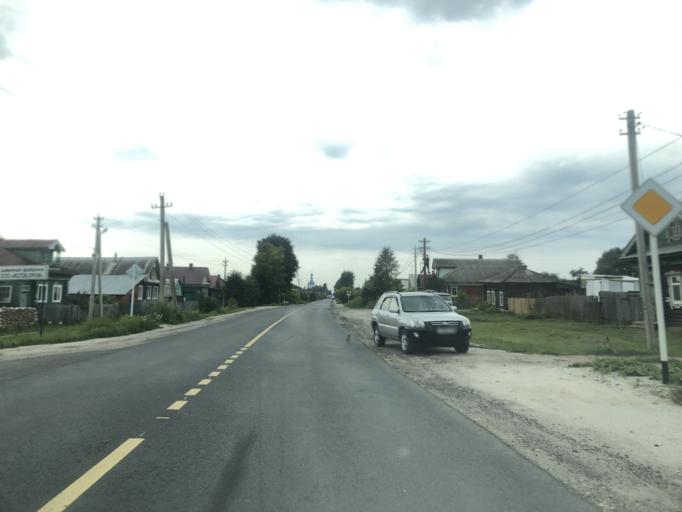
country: RU
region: Ivanovo
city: Pestyaki
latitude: 56.7054
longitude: 42.6797
